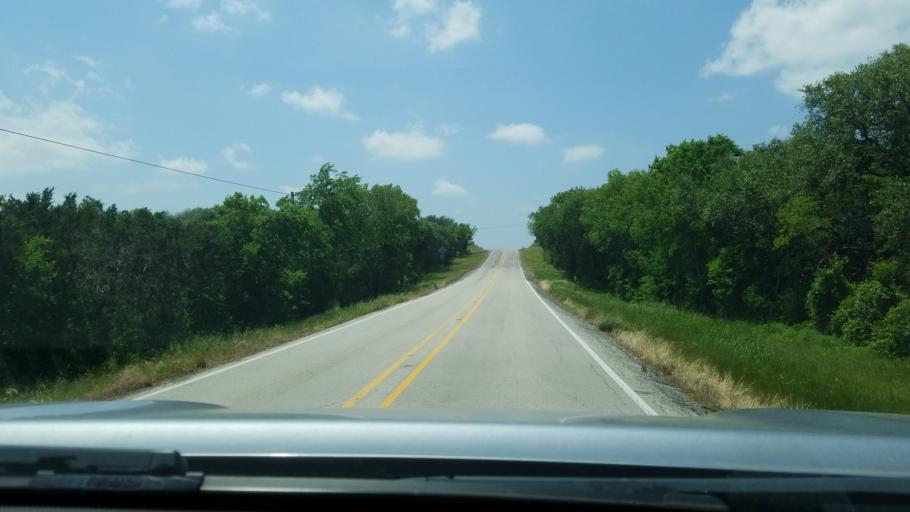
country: US
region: Texas
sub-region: Hays County
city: Woodcreek
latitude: 30.0983
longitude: -98.2424
